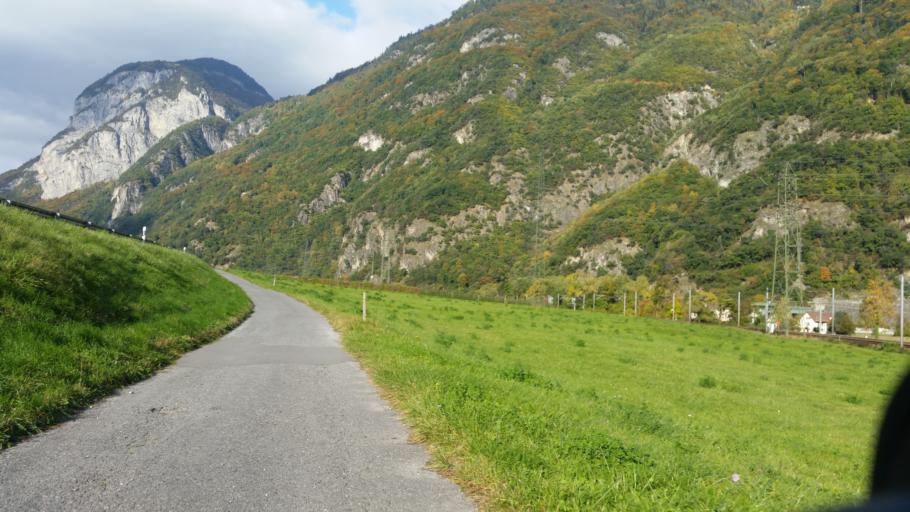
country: CH
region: Valais
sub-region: Martigny District
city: Evionnaz
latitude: 46.1814
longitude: 7.0294
